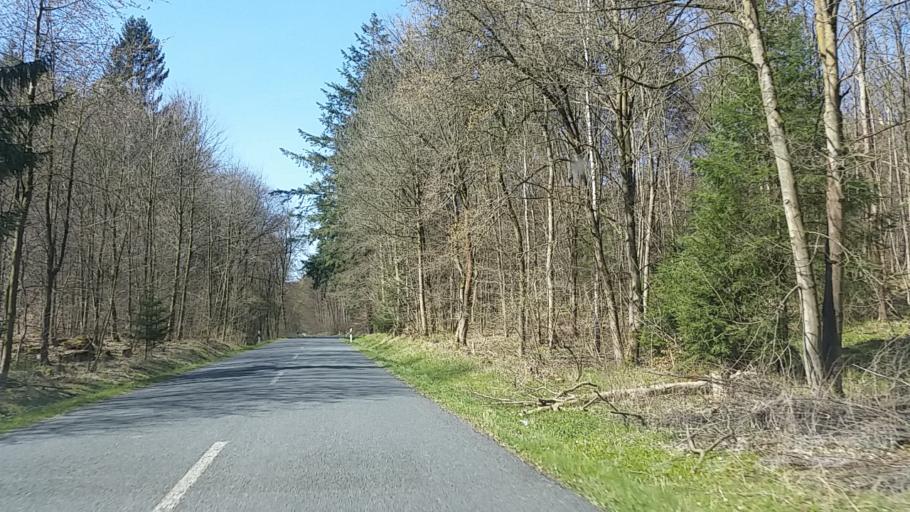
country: DE
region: Lower Saxony
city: Kneitlingen
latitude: 52.1956
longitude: 10.7785
